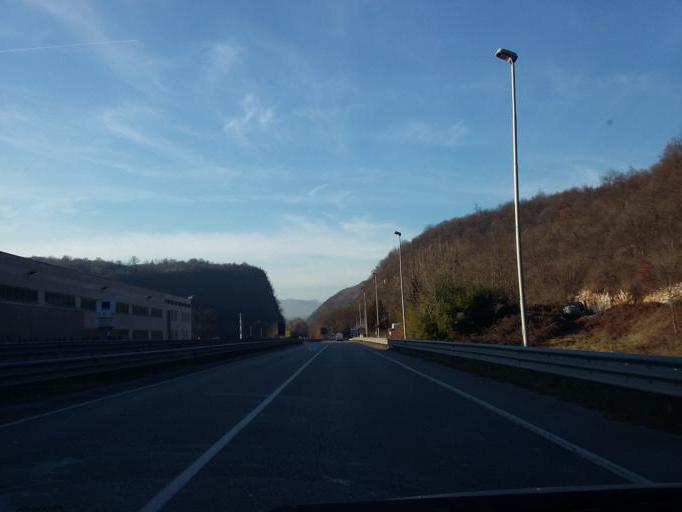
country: IT
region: Lombardy
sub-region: Provincia di Brescia
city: Sabbio Chiese
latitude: 45.6462
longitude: 10.4550
